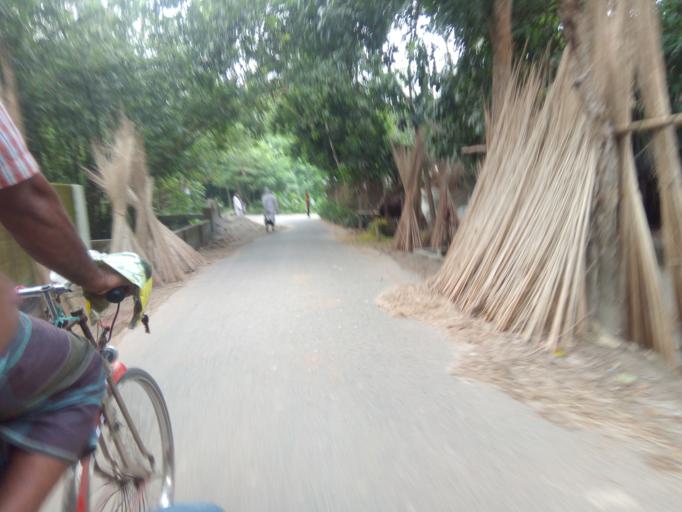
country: BD
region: Khulna
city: Kalia
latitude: 23.2161
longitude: 89.7048
